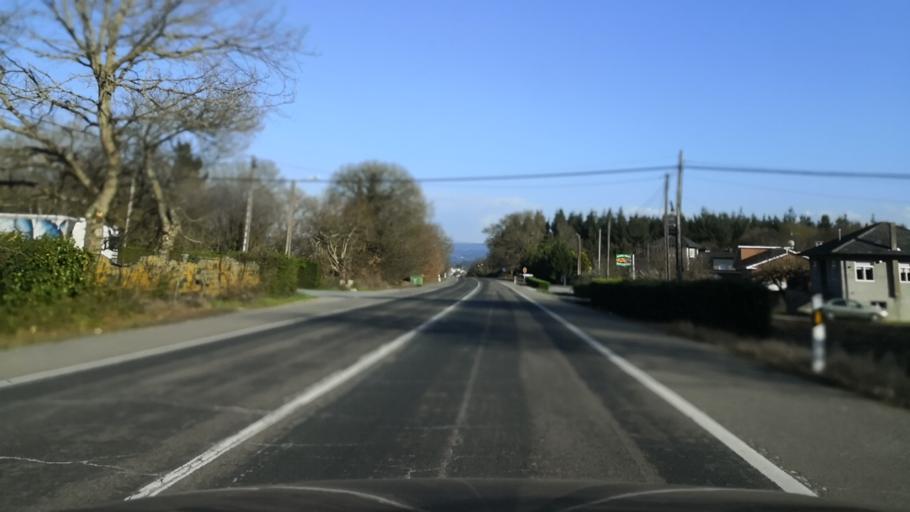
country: ES
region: Galicia
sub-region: Provincia de Lugo
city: Corgo
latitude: 42.9527
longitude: -7.4613
